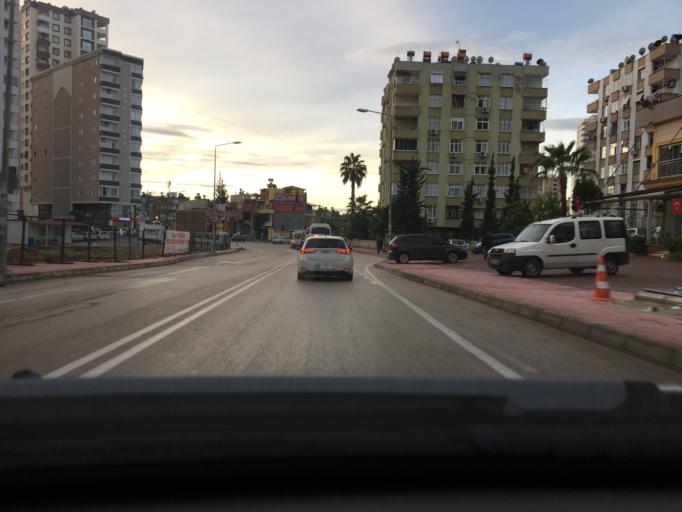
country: TR
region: Adana
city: Seyhan
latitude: 37.0239
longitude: 35.2918
